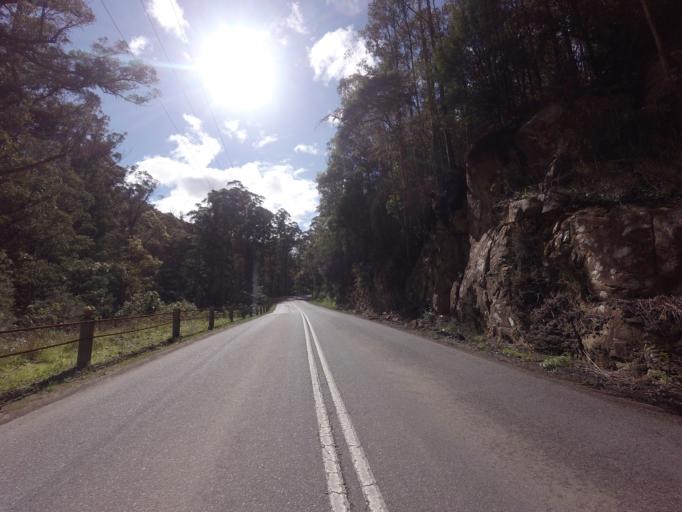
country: AU
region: Tasmania
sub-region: Huon Valley
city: Geeveston
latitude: -43.2317
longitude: 146.9890
